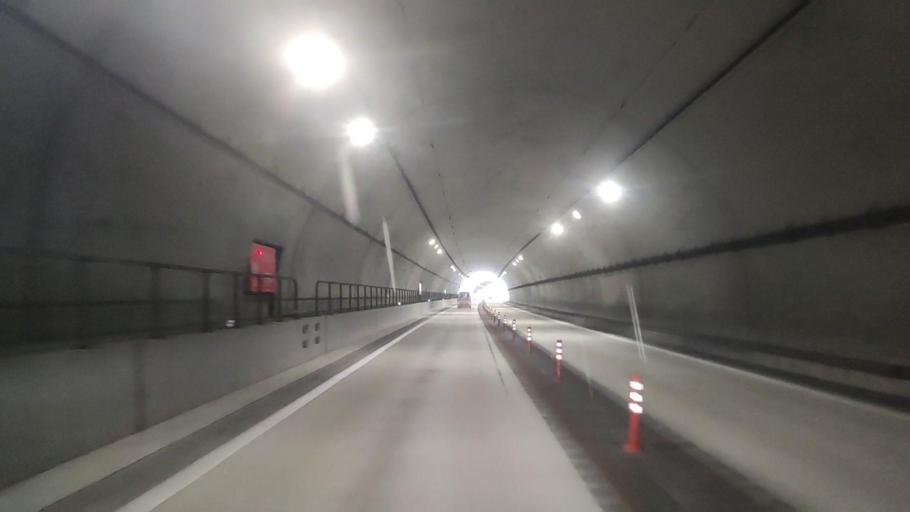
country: JP
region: Wakayama
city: Tanabe
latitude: 33.5955
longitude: 135.4352
